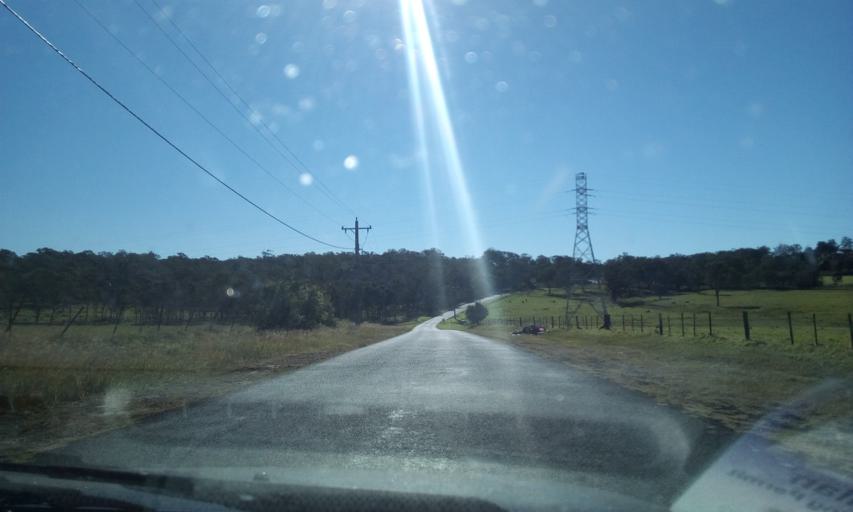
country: AU
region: New South Wales
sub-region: Wollongong
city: Dapto
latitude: -34.5233
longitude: 150.7786
